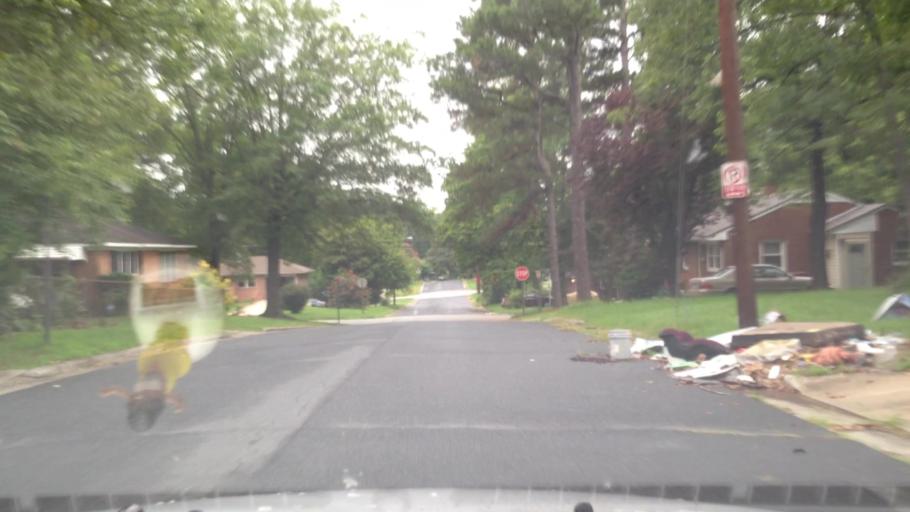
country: US
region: North Carolina
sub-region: Guilford County
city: Greensboro
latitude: 36.0515
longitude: -79.7627
